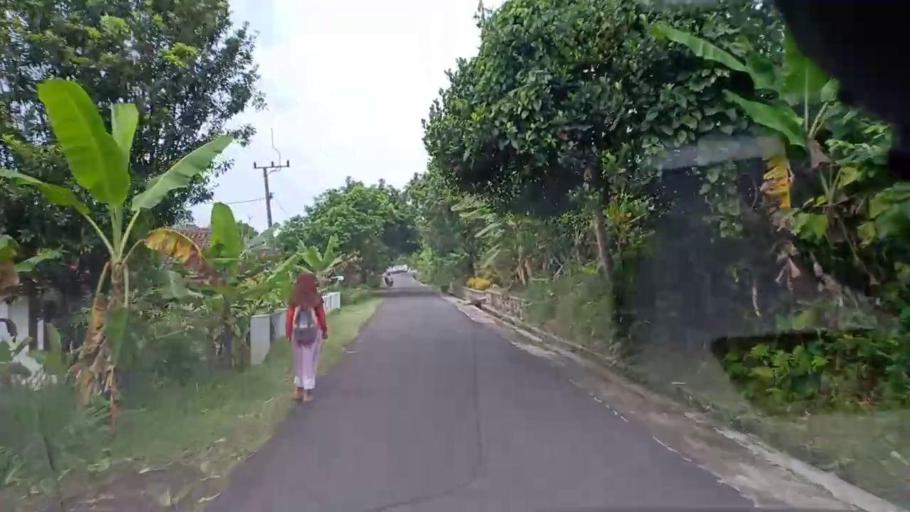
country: ID
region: West Java
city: Gerempay
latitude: -7.3375
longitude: 108.2954
